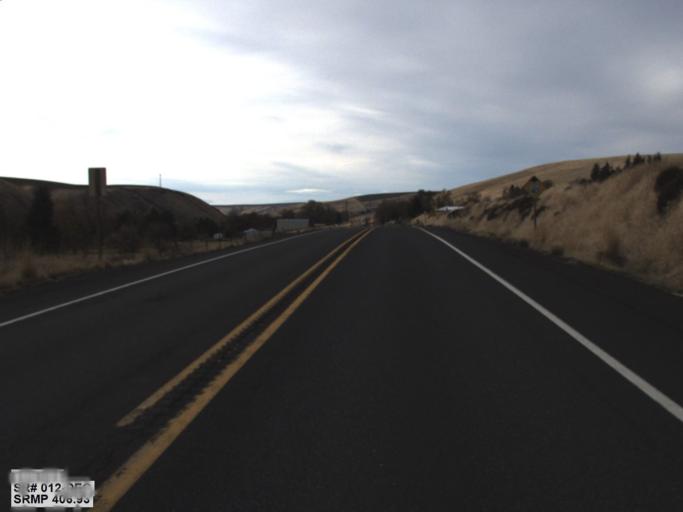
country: US
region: Washington
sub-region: Garfield County
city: Pomeroy
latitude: 46.4723
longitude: -117.5279
